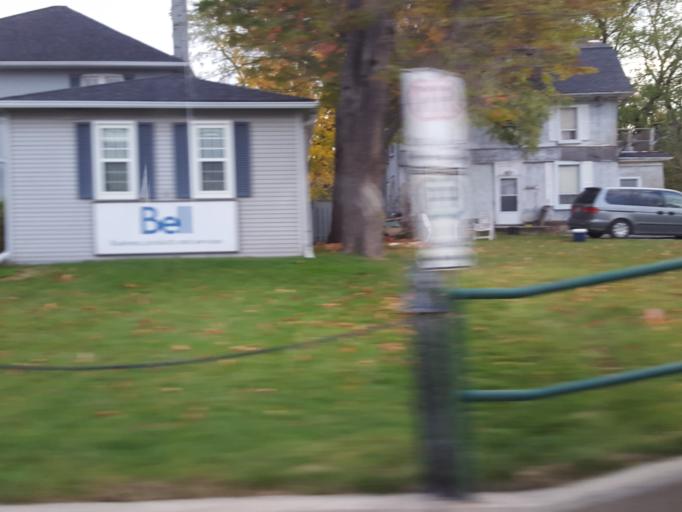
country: CA
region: Ontario
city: Newmarket
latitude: 44.0039
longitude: -79.4685
